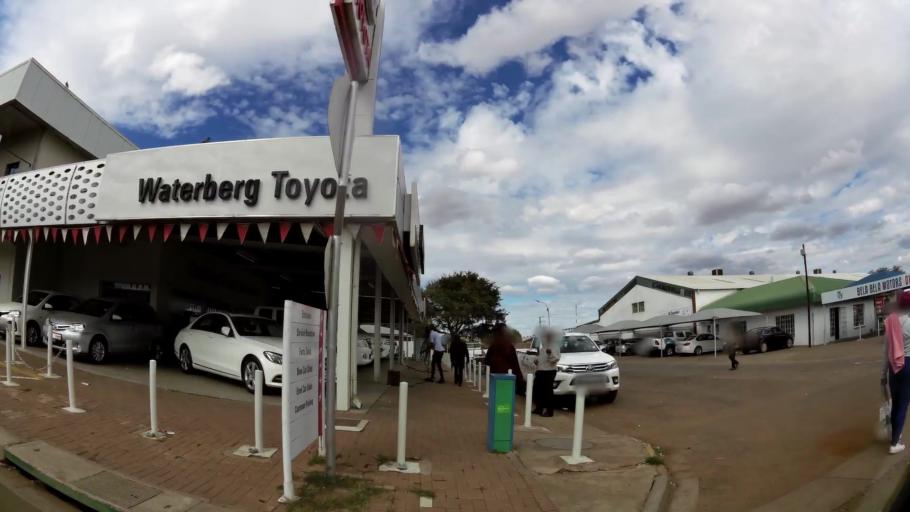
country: ZA
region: Limpopo
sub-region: Waterberg District Municipality
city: Bela-Bela
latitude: -24.8868
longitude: 28.2956
